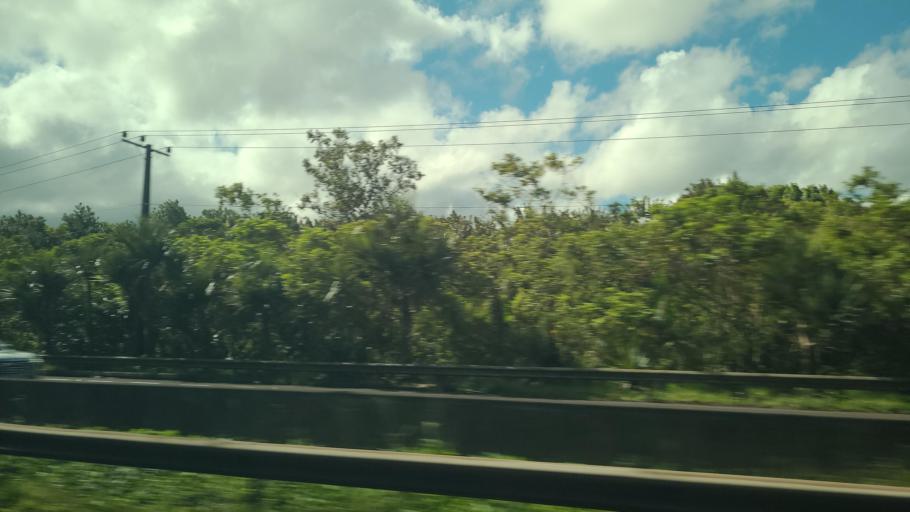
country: MU
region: Plaines Wilhems
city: Midlands
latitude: -20.3306
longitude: 57.5514
